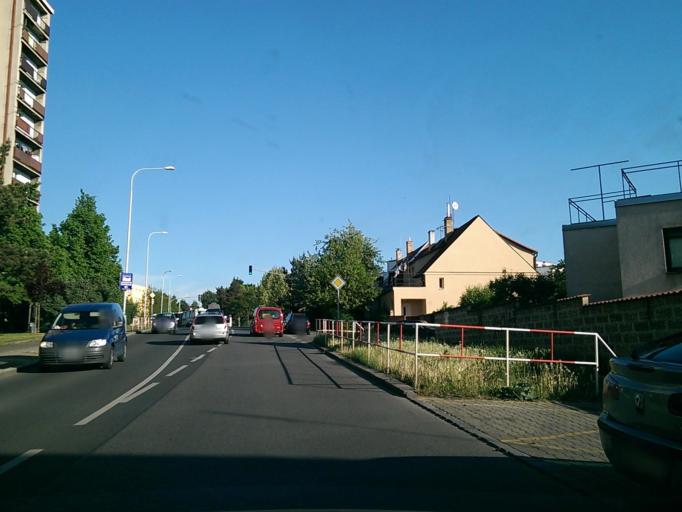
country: CZ
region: Praha
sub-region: Praha 8
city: Karlin
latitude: 50.0470
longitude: 14.4828
